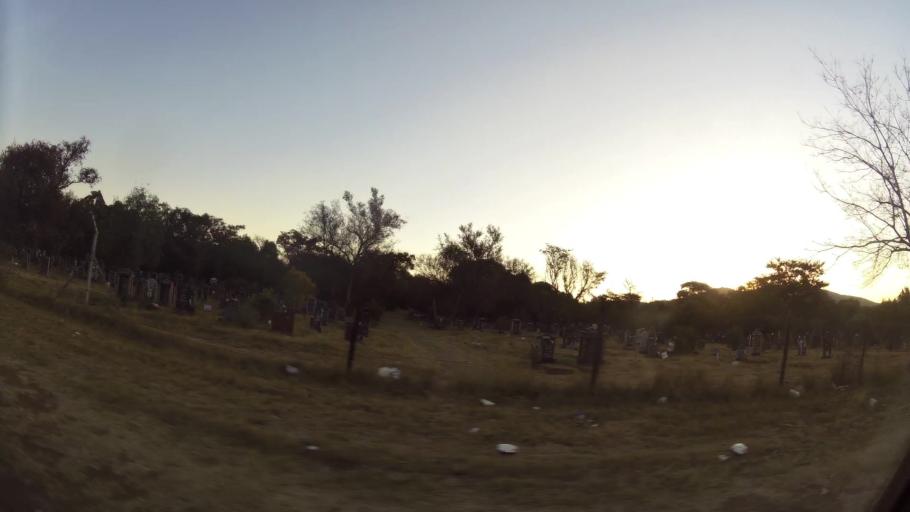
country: ZA
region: North-West
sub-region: Bojanala Platinum District Municipality
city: Rustenburg
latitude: -25.6696
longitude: 27.2171
